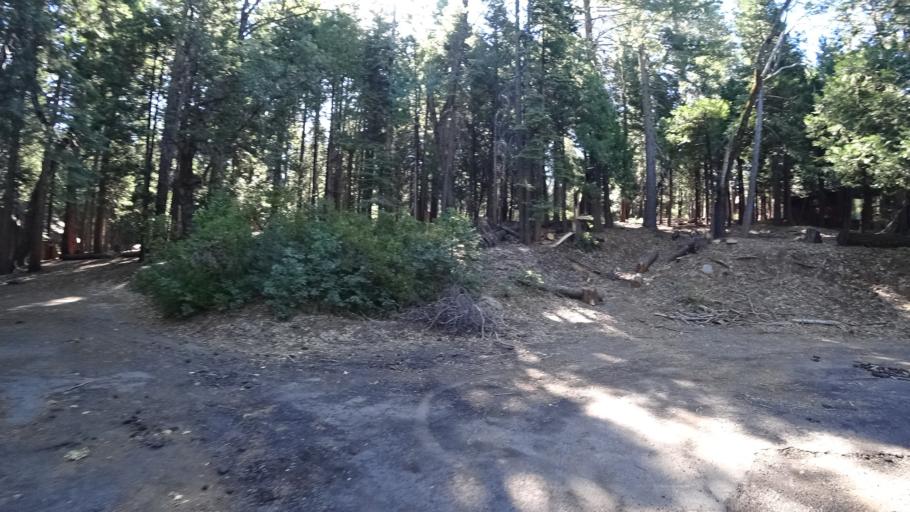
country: US
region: California
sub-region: Calaveras County
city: Arnold
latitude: 38.3058
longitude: -120.2711
